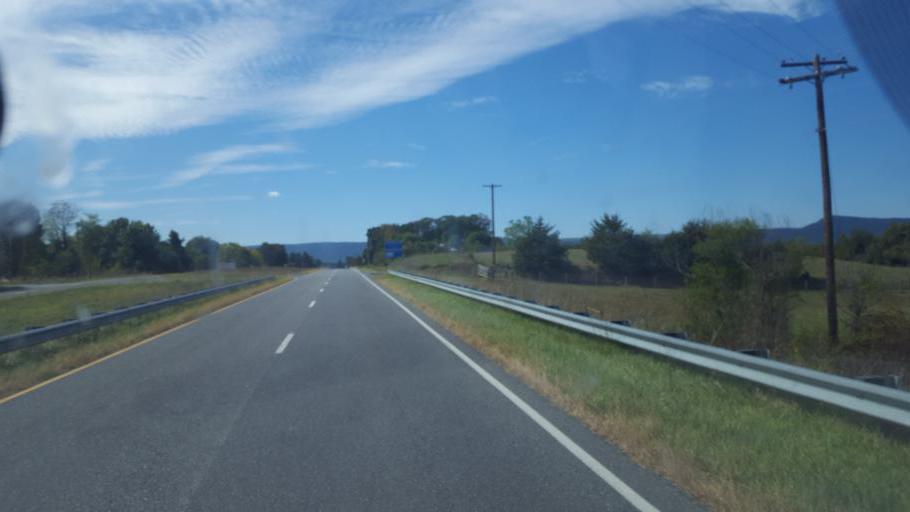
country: US
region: Virginia
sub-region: Page County
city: Luray
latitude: 38.6740
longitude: -78.3944
